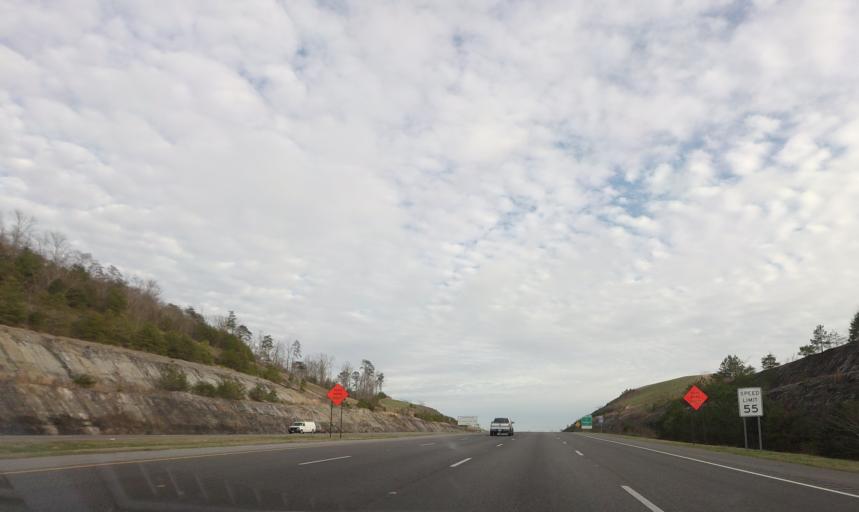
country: US
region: Alabama
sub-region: Jefferson County
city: Forestdale
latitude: 33.5933
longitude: -86.8796
